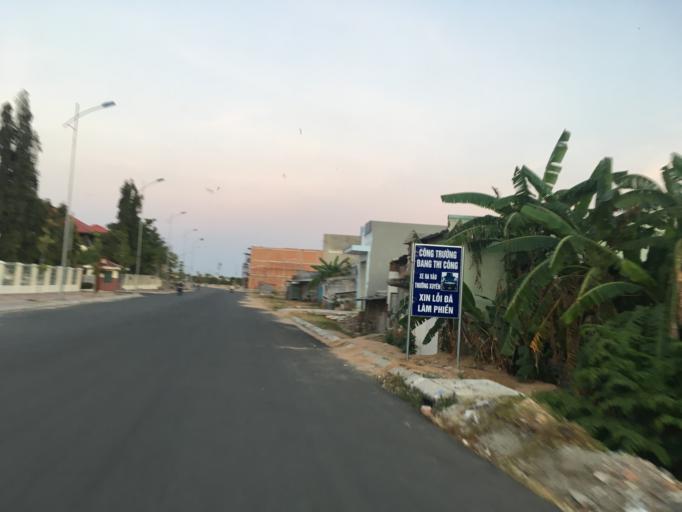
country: VN
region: Ninh Thuan
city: Phan Rang-Thap Cham
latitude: 11.5742
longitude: 108.9946
